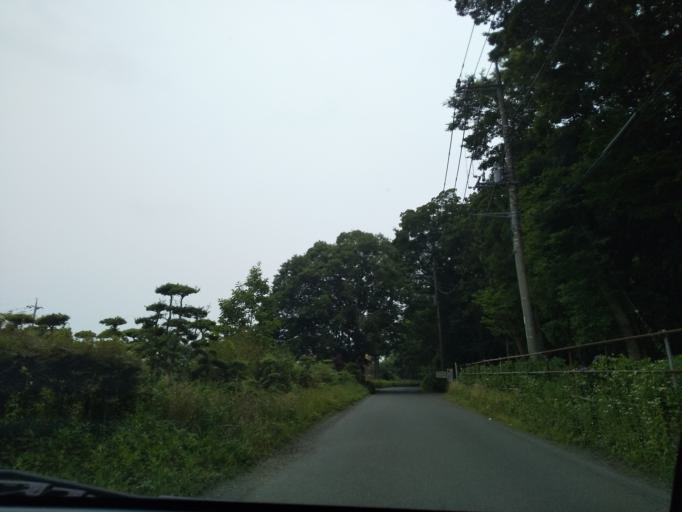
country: JP
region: Kanagawa
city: Zama
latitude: 35.5251
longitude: 139.3938
